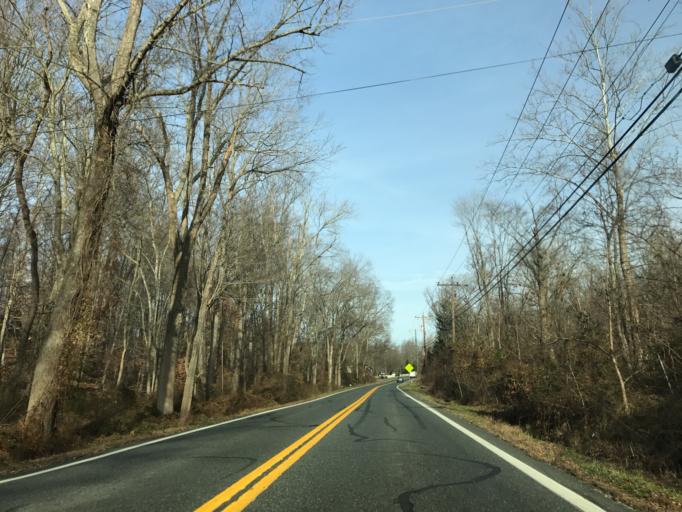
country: US
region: Maryland
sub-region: Harford County
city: Pleasant Hills
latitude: 39.4831
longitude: -76.4158
